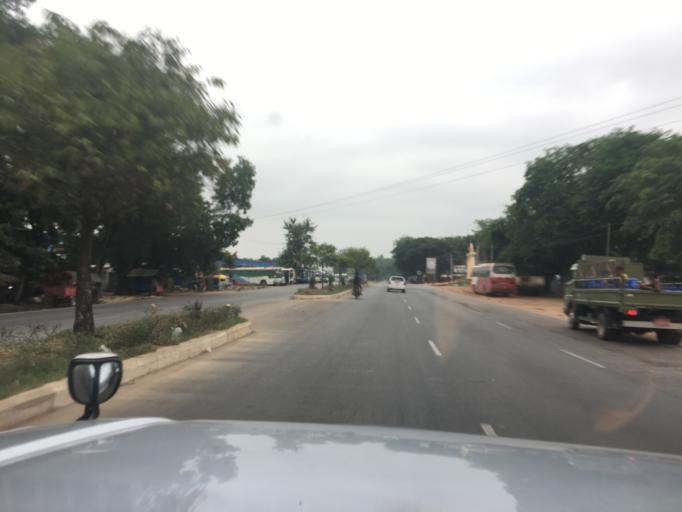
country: MM
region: Bago
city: Thanatpin
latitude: 17.1881
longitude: 96.3919
